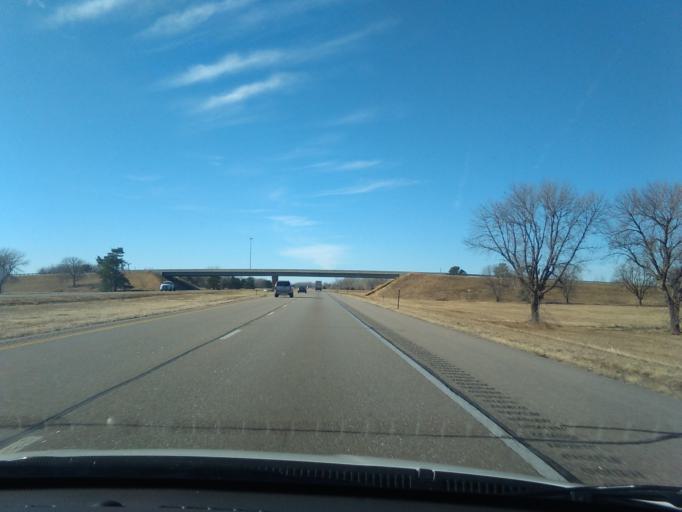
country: US
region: Nebraska
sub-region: Hall County
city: Wood River
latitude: 40.7637
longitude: -98.5858
